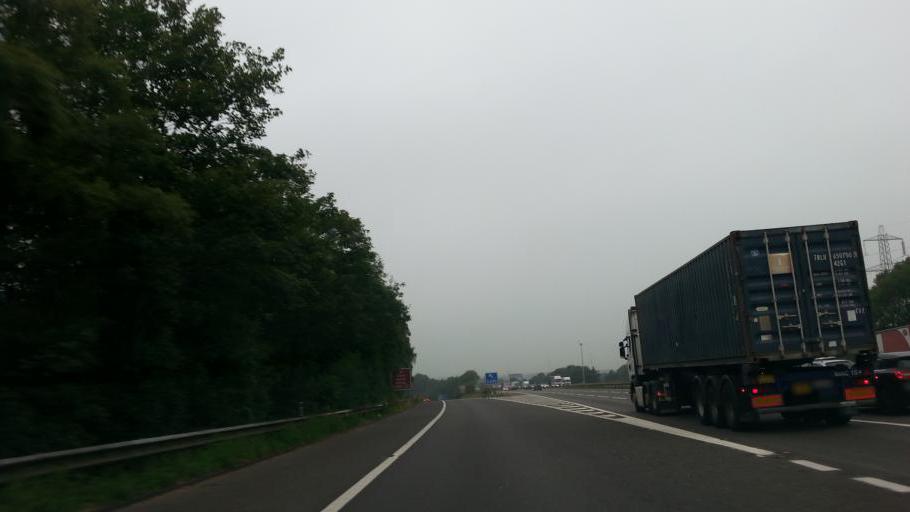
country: GB
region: England
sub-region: Warwickshire
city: Exhall
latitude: 52.4602
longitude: -1.4873
